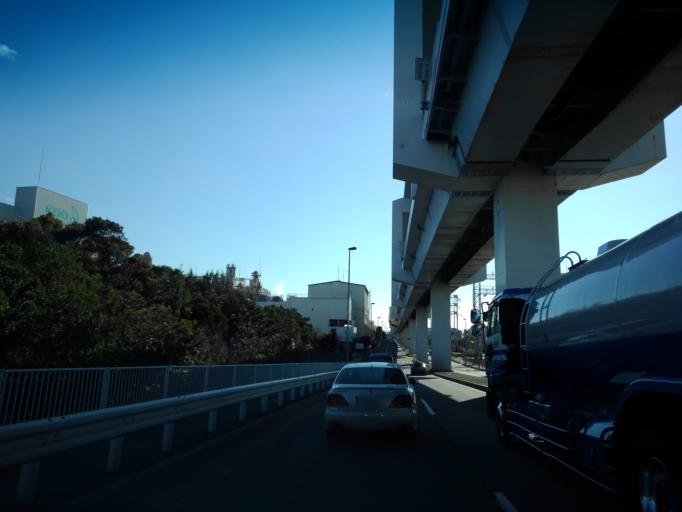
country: JP
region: Kanagawa
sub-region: Kawasaki-shi
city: Kawasaki
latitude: 35.5338
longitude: 139.7655
